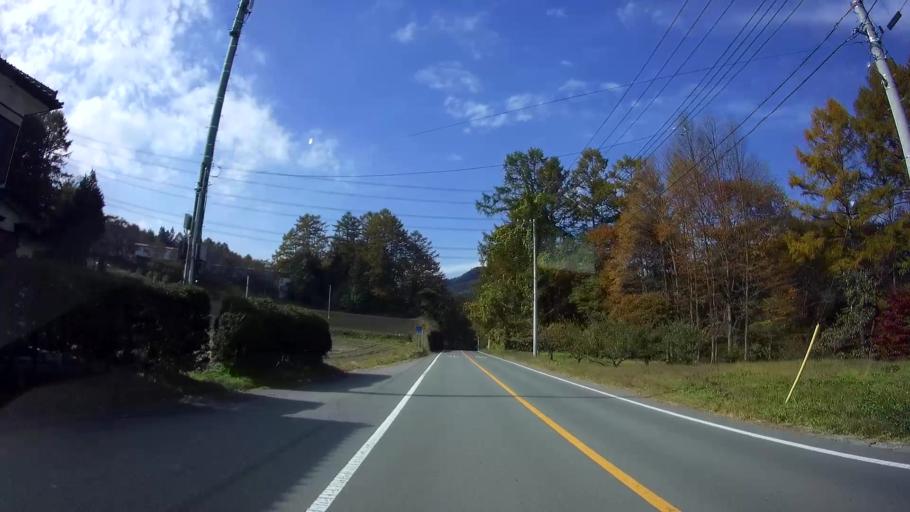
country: JP
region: Gunma
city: Nakanojomachi
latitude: 36.5065
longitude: 138.7413
